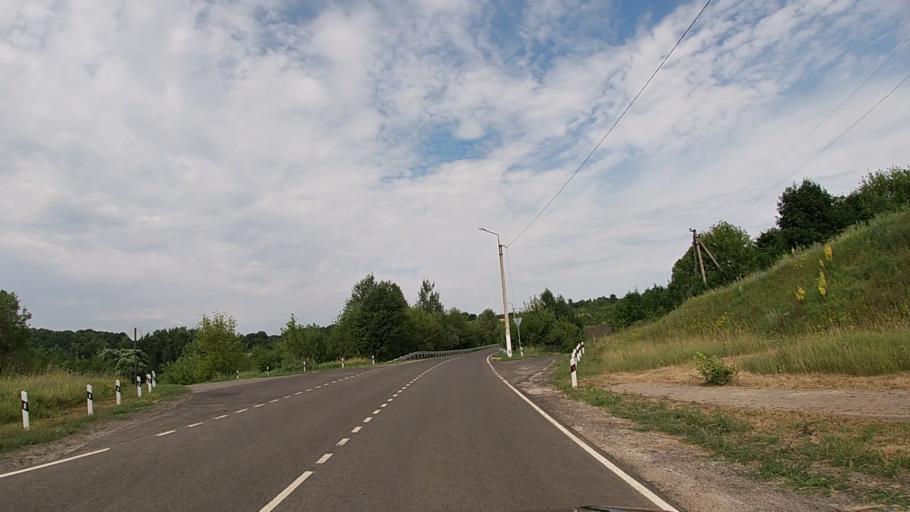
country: UA
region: Sumy
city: Krasnopillya
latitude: 50.8138
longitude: 35.4301
